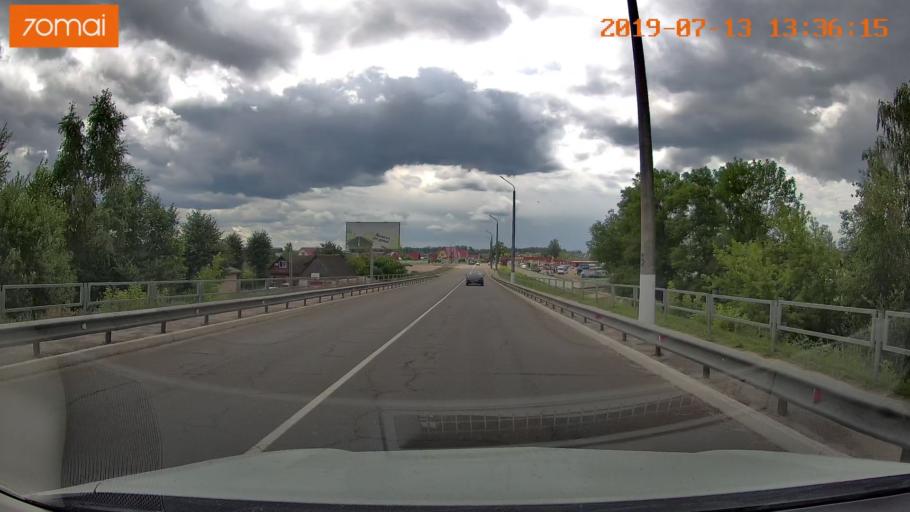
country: BY
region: Mogilev
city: Asipovichy
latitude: 53.3038
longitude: 28.6235
